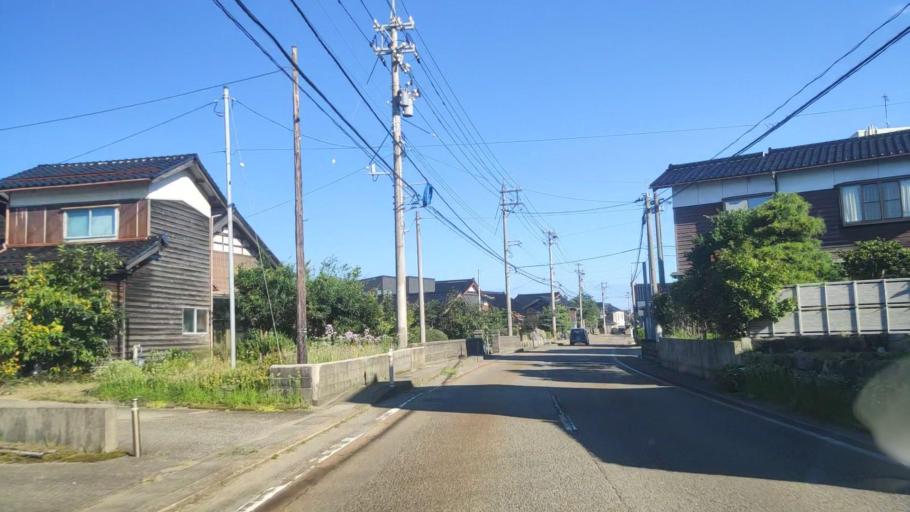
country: JP
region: Ishikawa
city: Hakui
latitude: 36.8214
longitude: 136.7566
